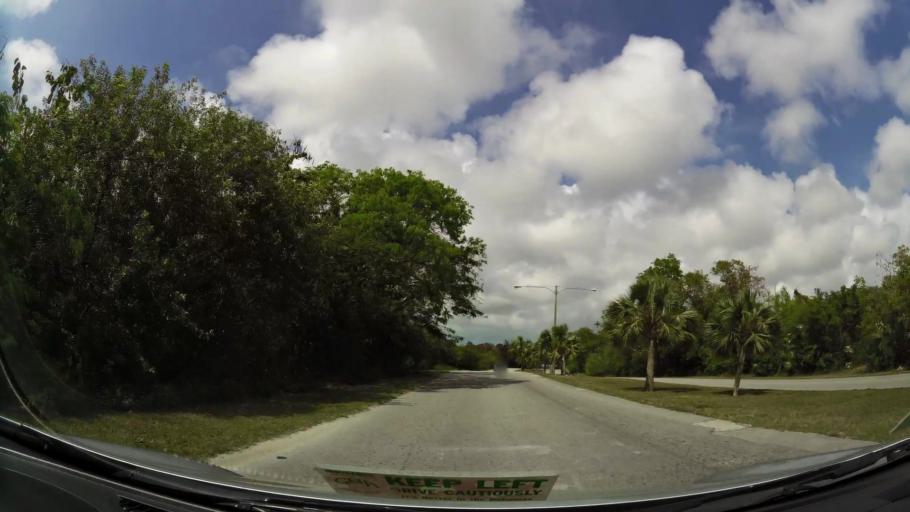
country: BS
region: Freeport
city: Freeport
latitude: 26.5097
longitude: -78.7093
